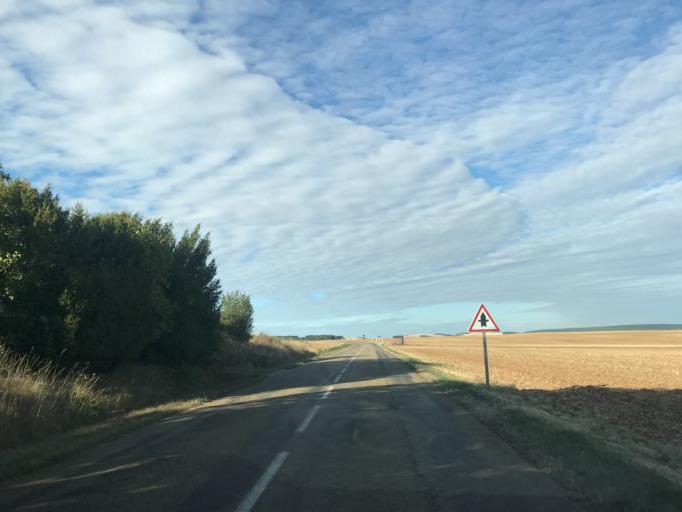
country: FR
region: Bourgogne
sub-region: Departement de l'Yonne
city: Fontenailles
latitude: 47.5898
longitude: 3.4718
